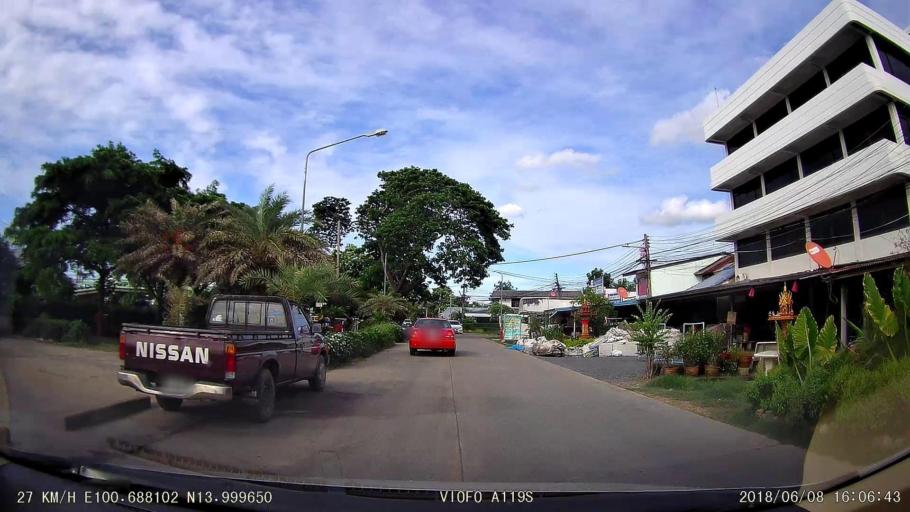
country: TH
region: Pathum Thani
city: Thanyaburi
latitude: 13.9997
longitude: 100.6882
